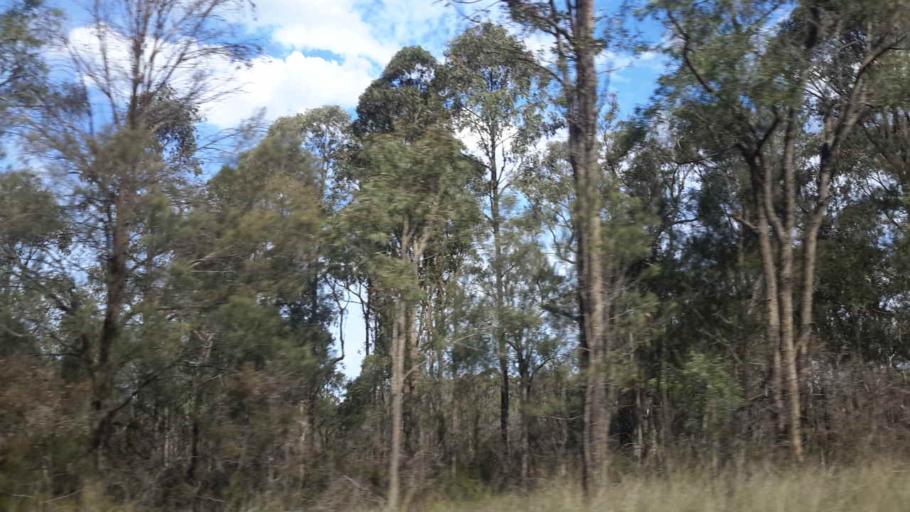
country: AU
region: New South Wales
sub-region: Hawkesbury
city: Richmond
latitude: -33.6717
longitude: 150.7515
